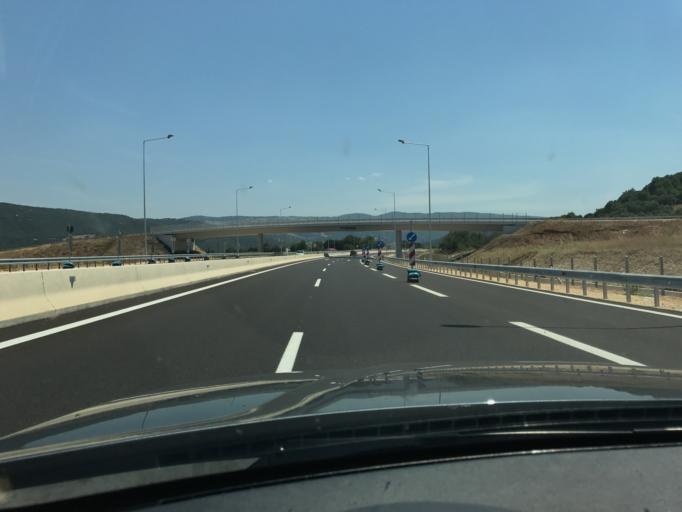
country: GR
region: Epirus
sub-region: Nomos Ioanninon
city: Agia Kyriaki
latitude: 39.5448
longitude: 20.8562
